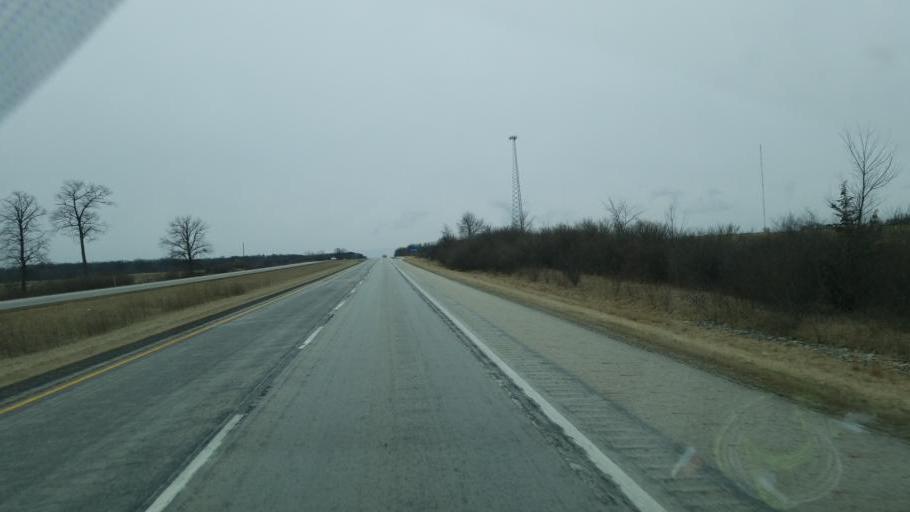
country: US
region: Indiana
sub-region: Fulton County
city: Rochester
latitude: 41.1460
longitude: -86.2400
